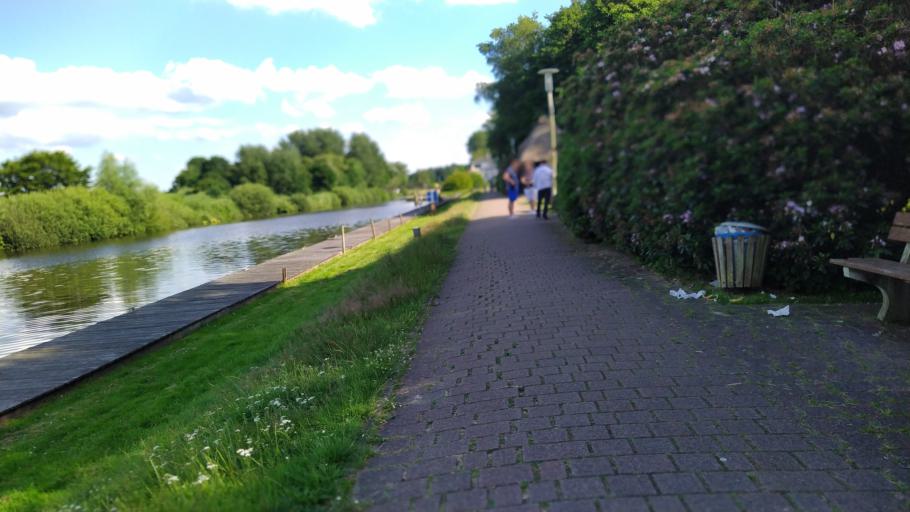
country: DE
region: Lower Saxony
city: Lintig
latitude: 53.6273
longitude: 8.8448
